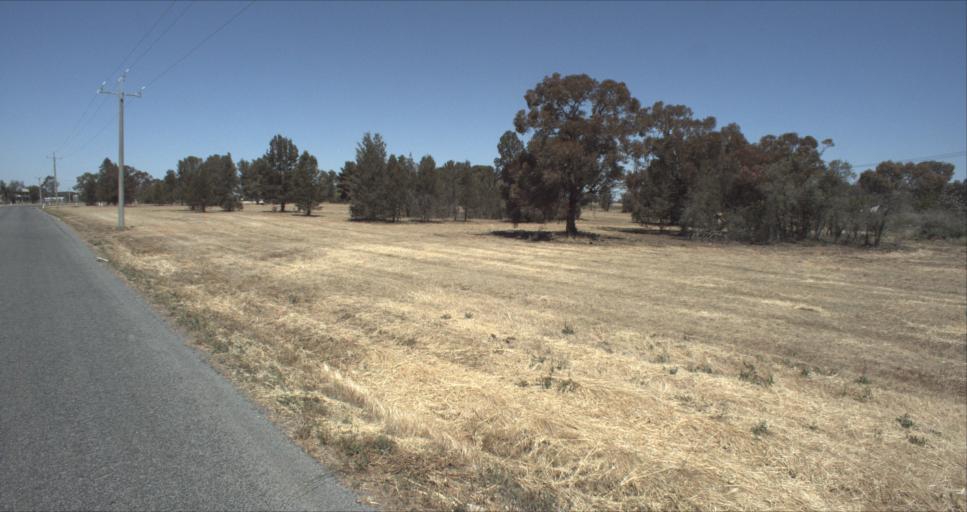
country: AU
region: New South Wales
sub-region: Leeton
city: Leeton
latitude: -34.5234
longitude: 146.4419
